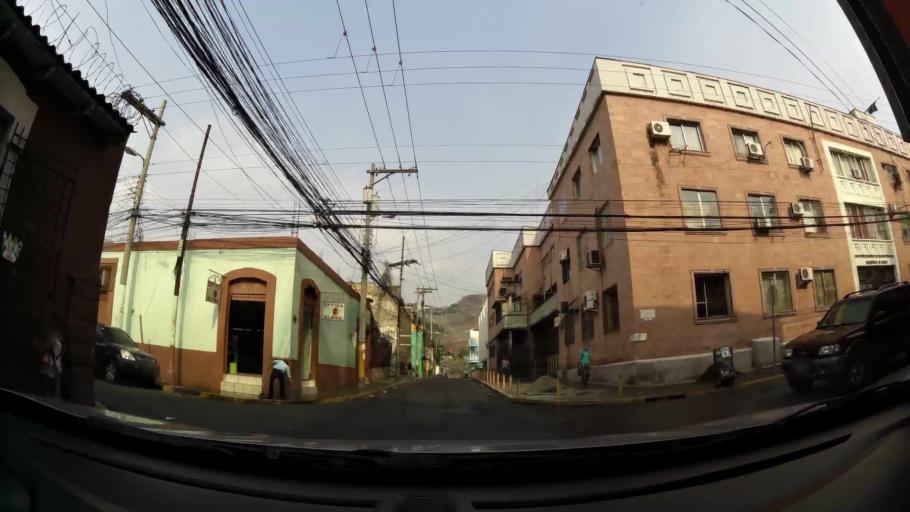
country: HN
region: Francisco Morazan
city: Tegucigalpa
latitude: 14.1057
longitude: -87.2078
